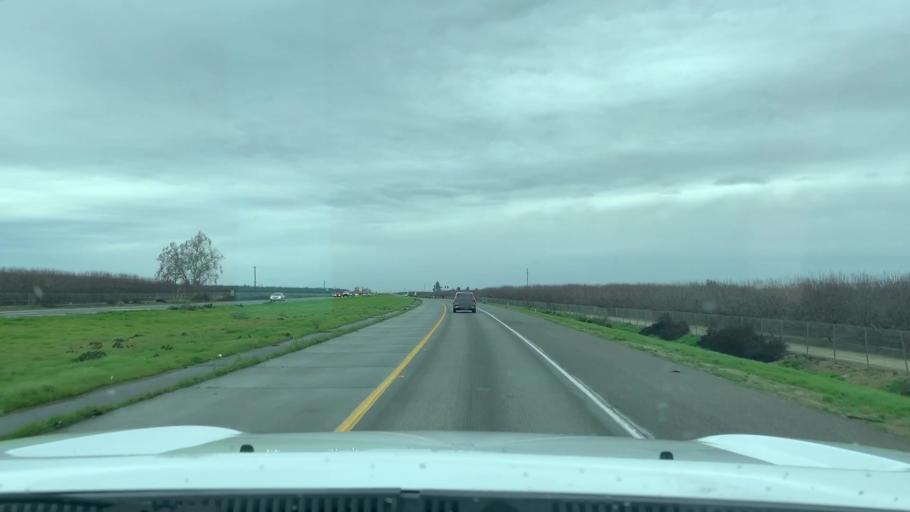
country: US
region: California
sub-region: Fresno County
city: Caruthers
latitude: 36.4979
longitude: -119.7862
